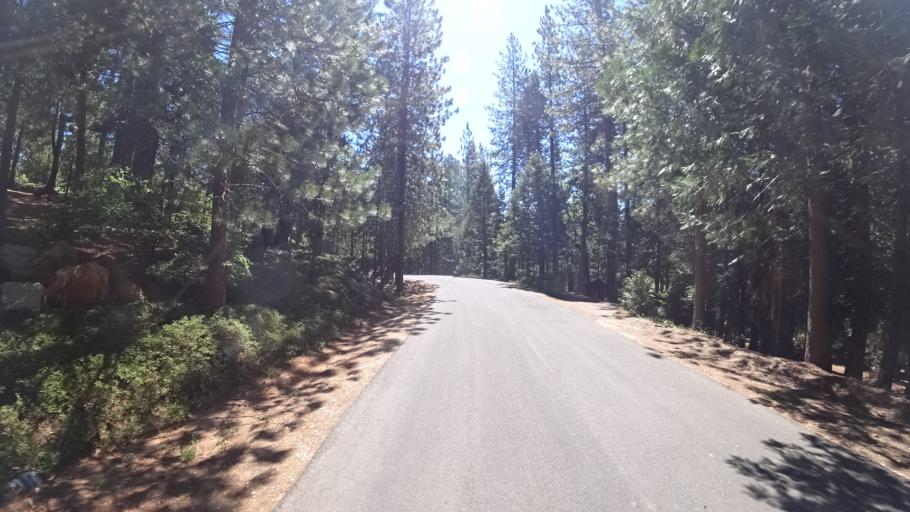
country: US
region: California
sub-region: Calaveras County
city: Arnold
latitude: 38.2866
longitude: -120.2772
